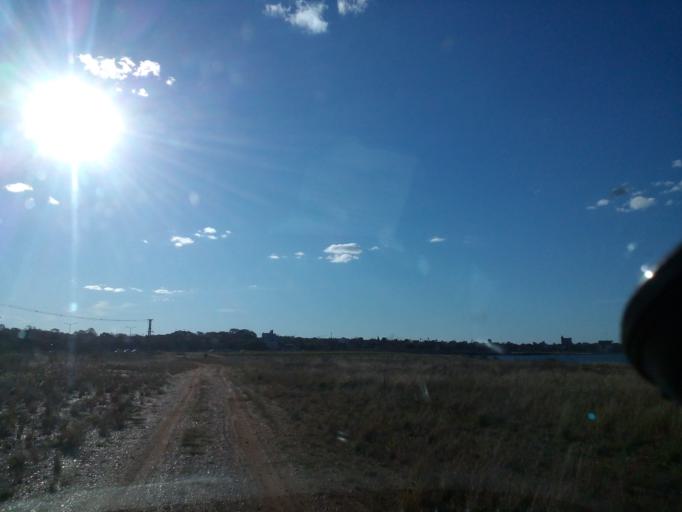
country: AR
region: Misiones
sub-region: Departamento de Capital
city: Posadas
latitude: -27.4109
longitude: -55.8885
